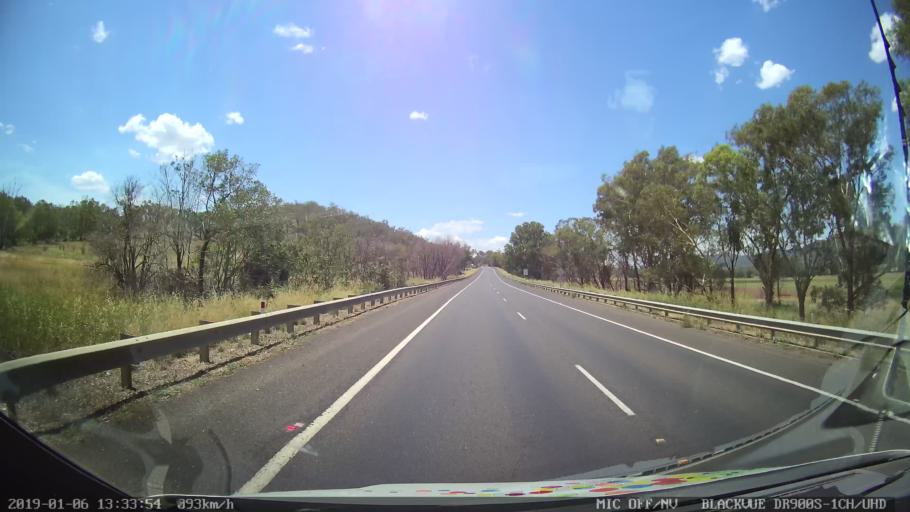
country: AU
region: New South Wales
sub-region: Tamworth Municipality
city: Kootingal
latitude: -31.0941
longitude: 151.0111
